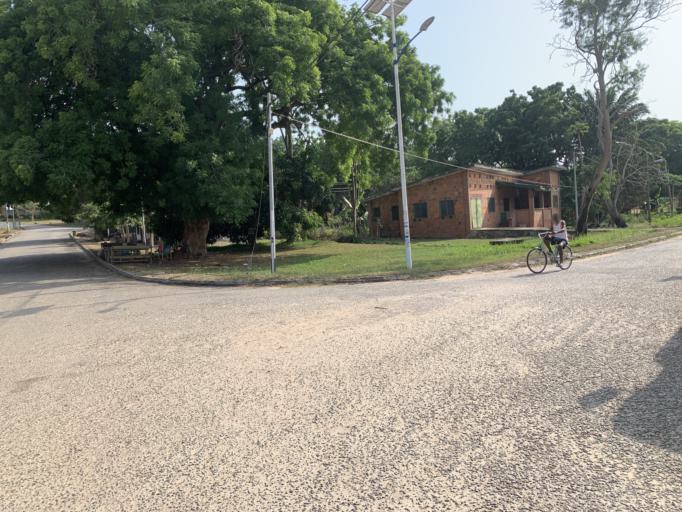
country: GH
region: Central
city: Winneba
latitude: 5.3398
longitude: -0.6274
